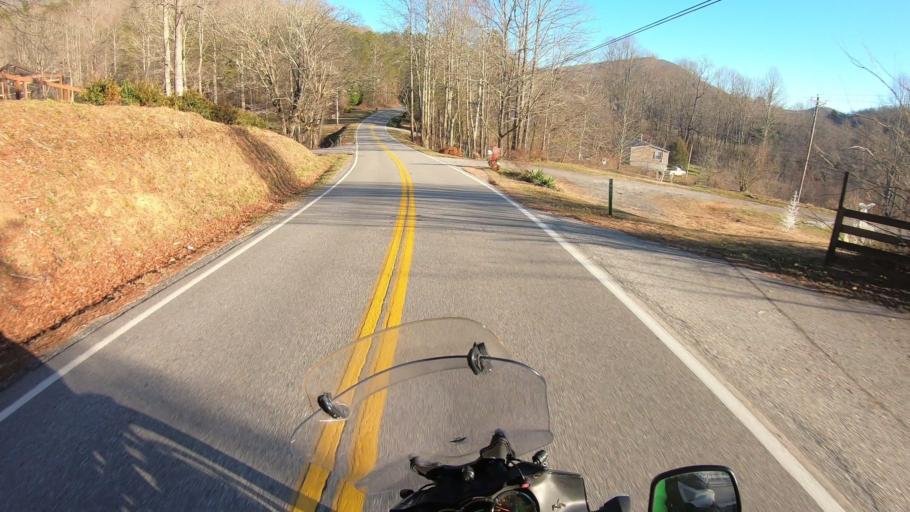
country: US
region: Georgia
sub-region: Lumpkin County
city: Dahlonega
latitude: 34.7064
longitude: -84.0404
